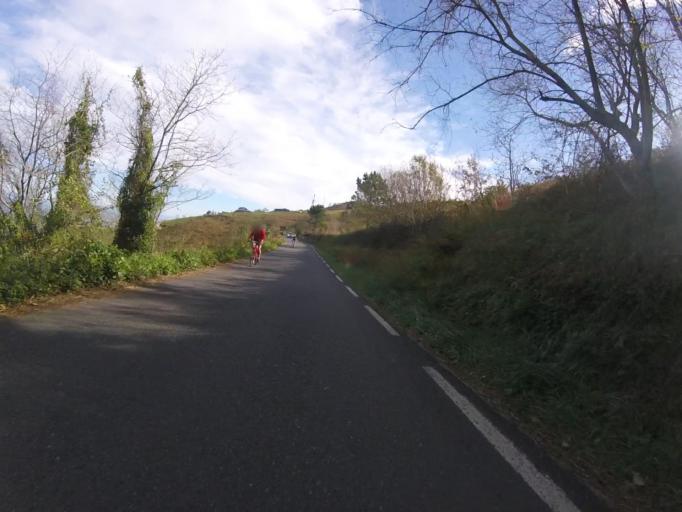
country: ES
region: Basque Country
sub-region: Provincia de Guipuzcoa
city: Usurbil
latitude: 43.2975
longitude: -2.0738
